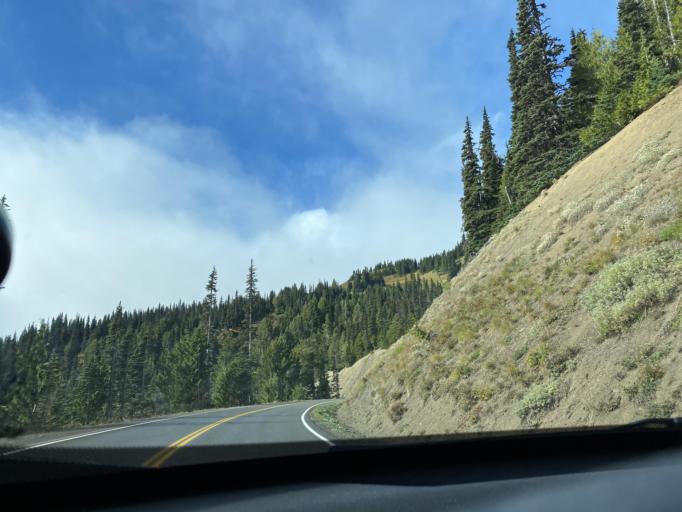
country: US
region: Washington
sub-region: Clallam County
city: Port Angeles
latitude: 47.9780
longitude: -123.4732
